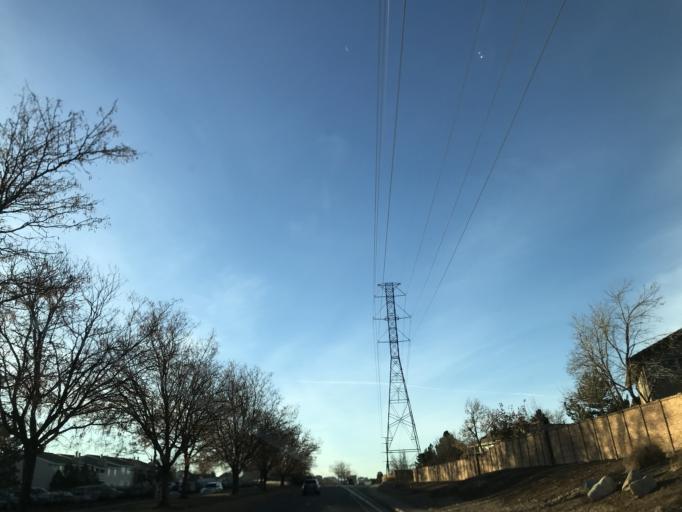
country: US
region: Colorado
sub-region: Arapahoe County
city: Glendale
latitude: 39.6709
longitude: -104.9038
